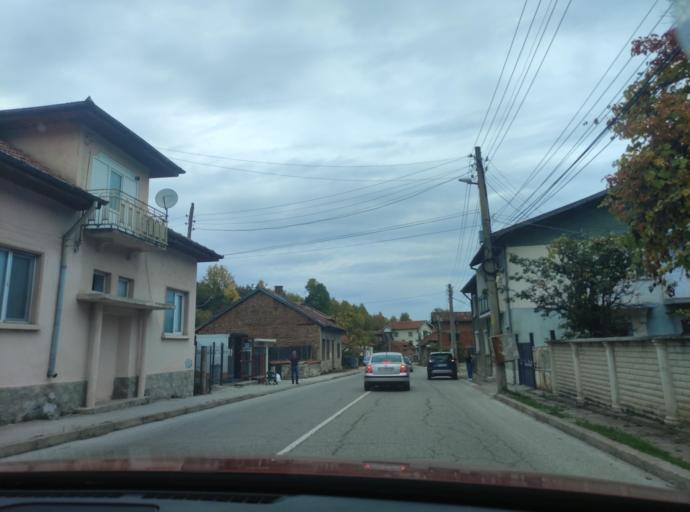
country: BG
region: Montana
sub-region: Obshtina Berkovitsa
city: Berkovitsa
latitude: 43.1951
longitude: 23.1608
